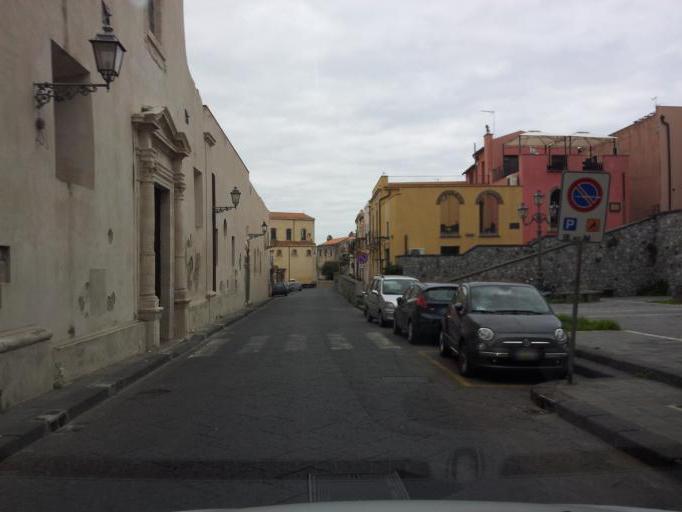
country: IT
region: Sicily
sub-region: Messina
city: Milazzo
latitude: 38.2300
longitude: 15.2433
